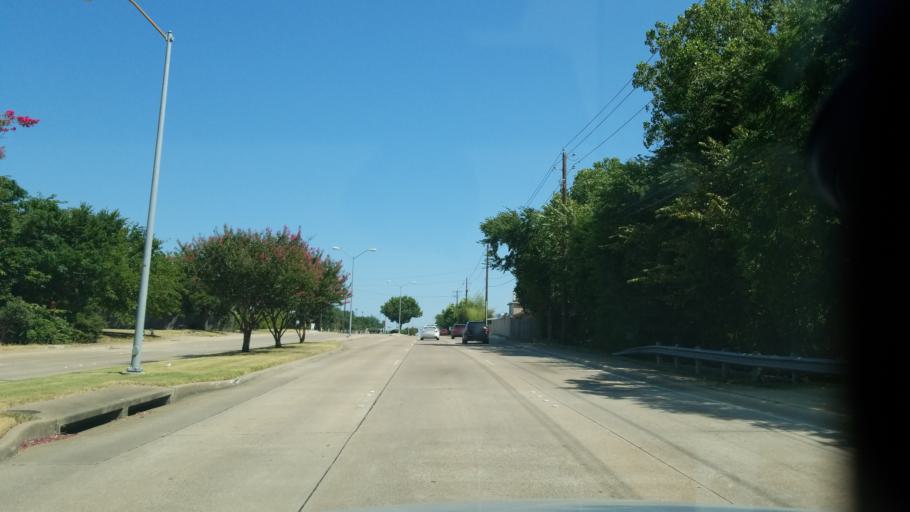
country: US
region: Texas
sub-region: Dallas County
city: Duncanville
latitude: 32.6363
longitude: -96.8913
